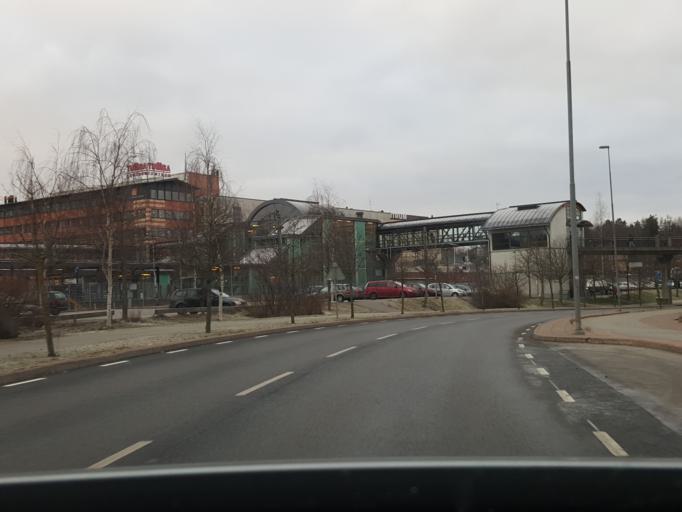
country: SE
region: Stockholm
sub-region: Botkyrka Kommun
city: Tumba
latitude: 59.2003
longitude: 17.8371
